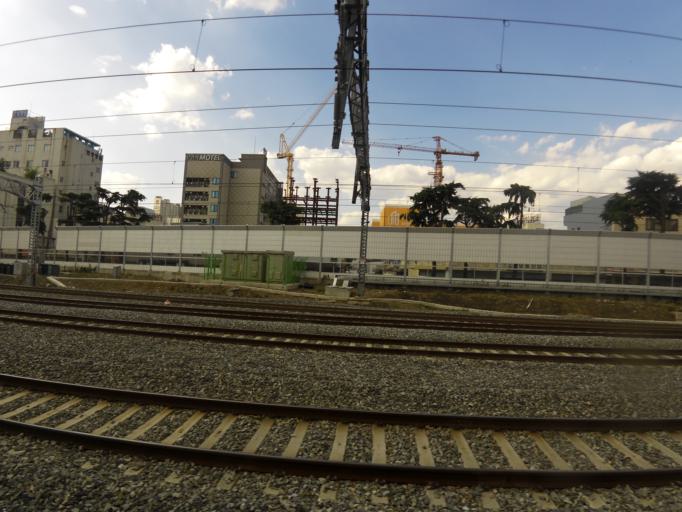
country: KR
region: Daegu
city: Daegu
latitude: 35.8755
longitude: 128.5986
